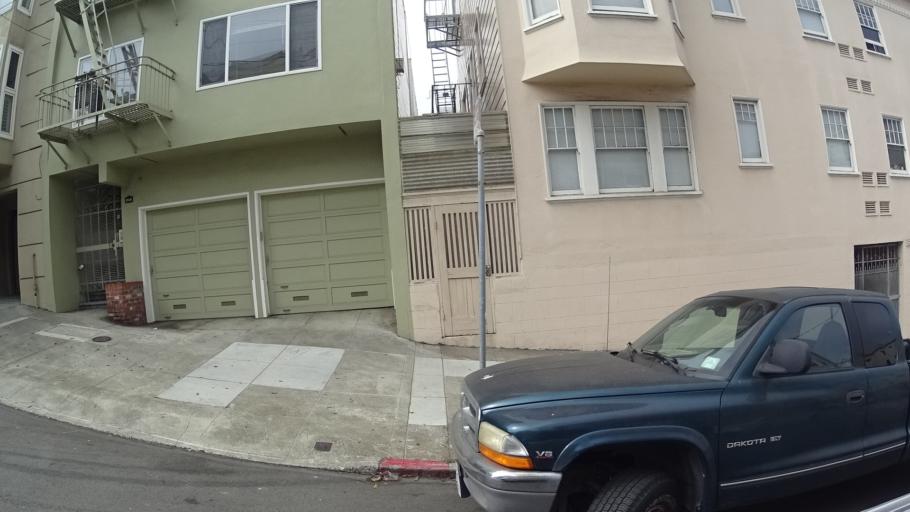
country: US
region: California
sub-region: San Francisco County
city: San Francisco
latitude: 37.7988
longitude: -122.4274
